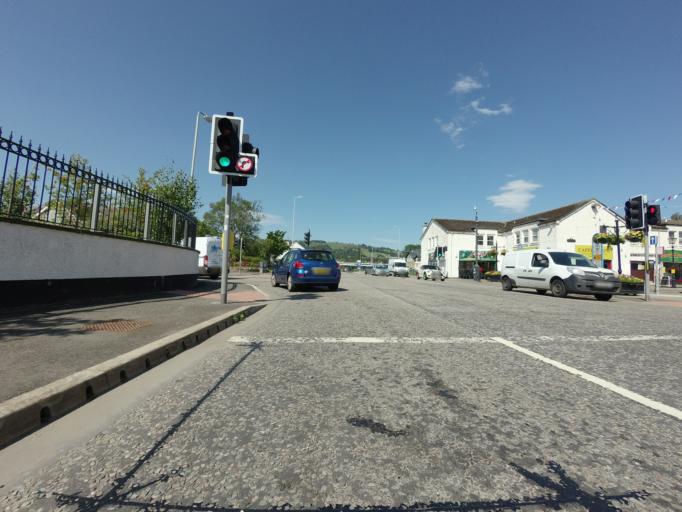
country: GB
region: Scotland
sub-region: Highland
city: Dingwall
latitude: 57.5954
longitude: -4.4314
